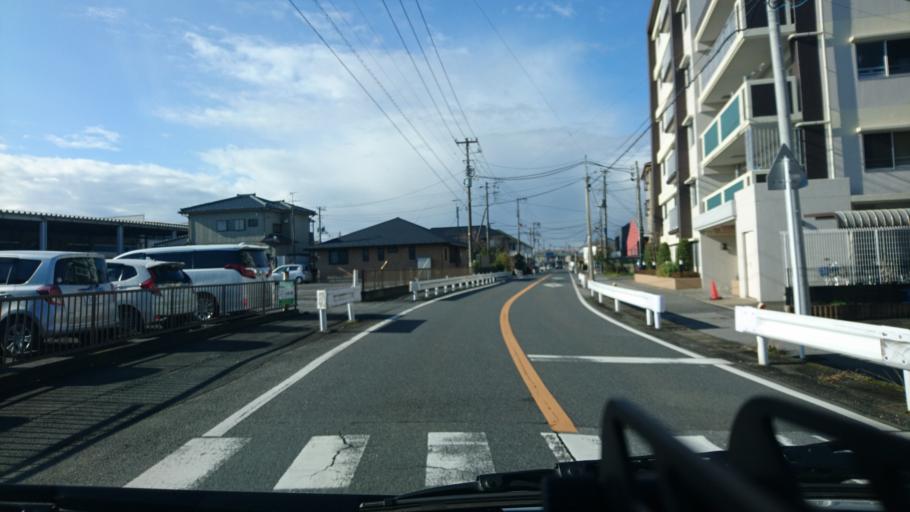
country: JP
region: Chiba
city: Kisarazu
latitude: 35.3705
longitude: 139.9234
